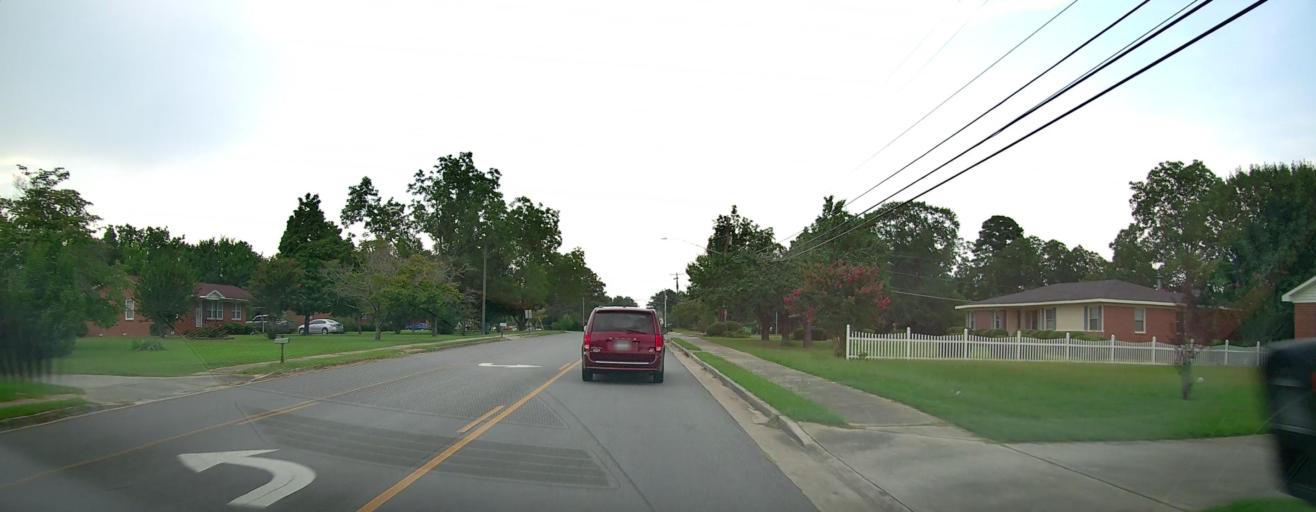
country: US
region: Georgia
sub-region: Laurens County
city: Dublin
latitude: 32.5625
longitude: -82.9129
